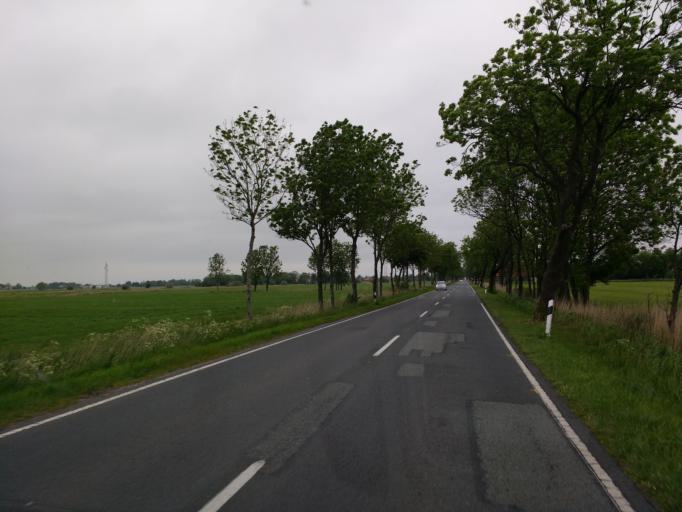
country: DE
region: Lower Saxony
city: Jever
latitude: 53.6514
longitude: 7.9180
